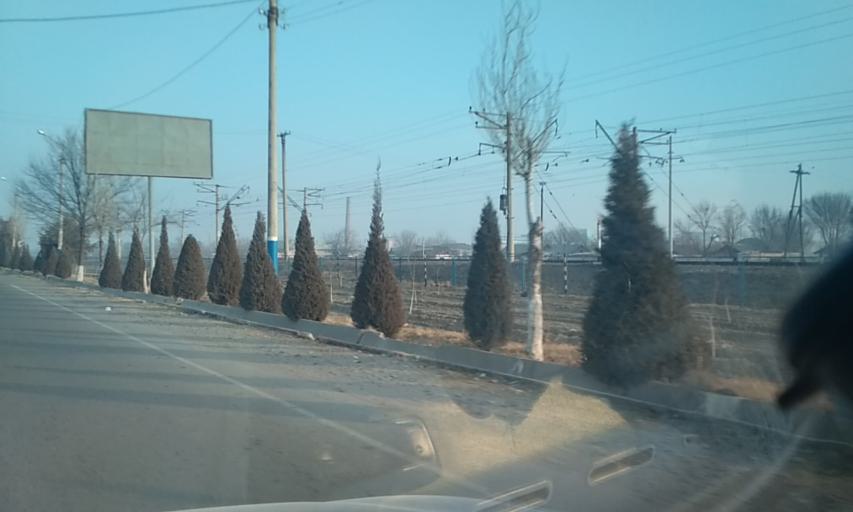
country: UZ
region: Sirdaryo
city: Guliston
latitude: 40.5108
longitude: 68.7598
